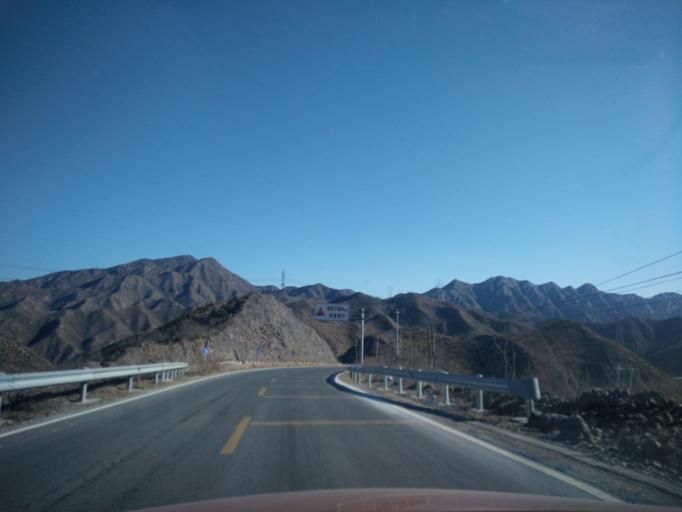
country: CN
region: Beijing
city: Zhaitang
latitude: 40.0281
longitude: 115.7064
